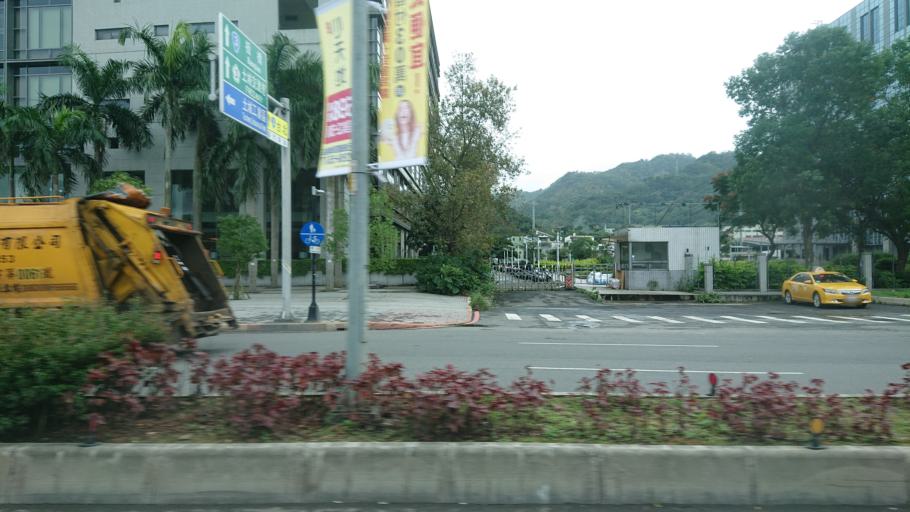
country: TW
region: Taipei
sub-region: Taipei
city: Banqiao
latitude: 24.9612
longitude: 121.4214
